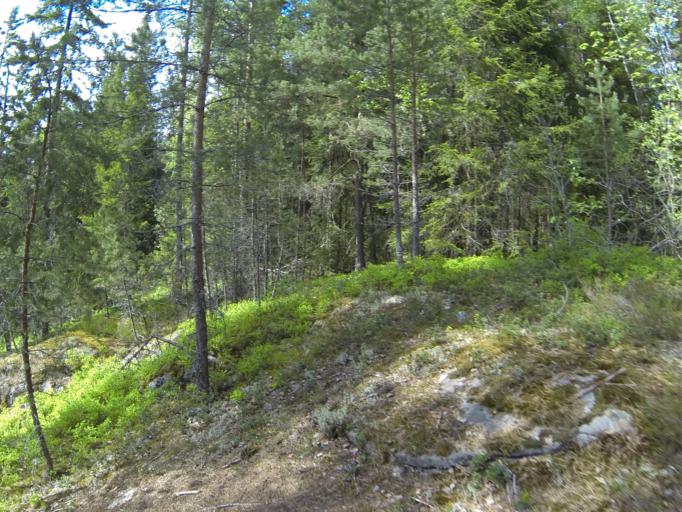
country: FI
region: Varsinais-Suomi
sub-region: Salo
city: Salo
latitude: 60.3857
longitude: 23.1743
